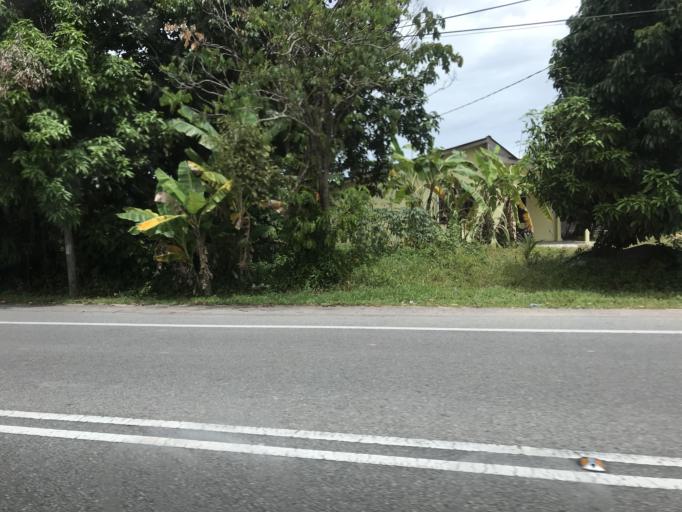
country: MY
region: Kelantan
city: Tumpat
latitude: 6.1747
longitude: 102.1827
